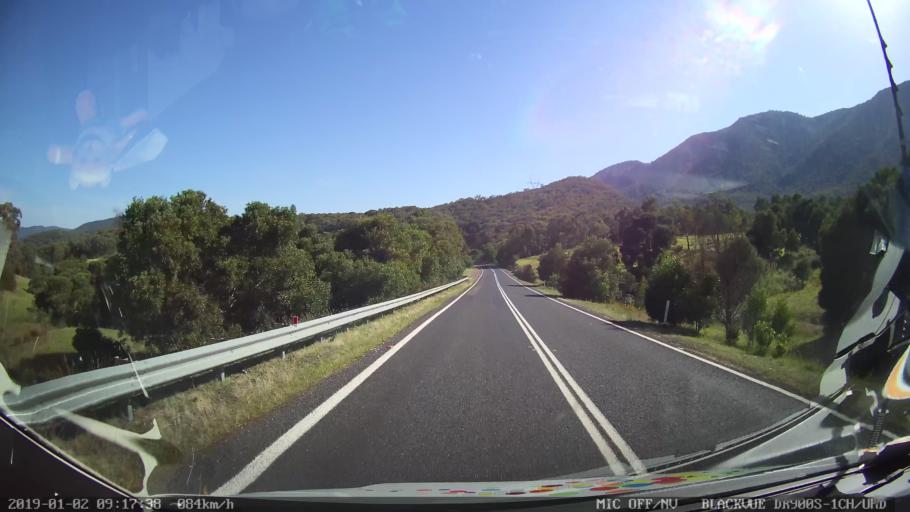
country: AU
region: New South Wales
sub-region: Tumut Shire
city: Tumut
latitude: -35.4376
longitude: 148.2864
